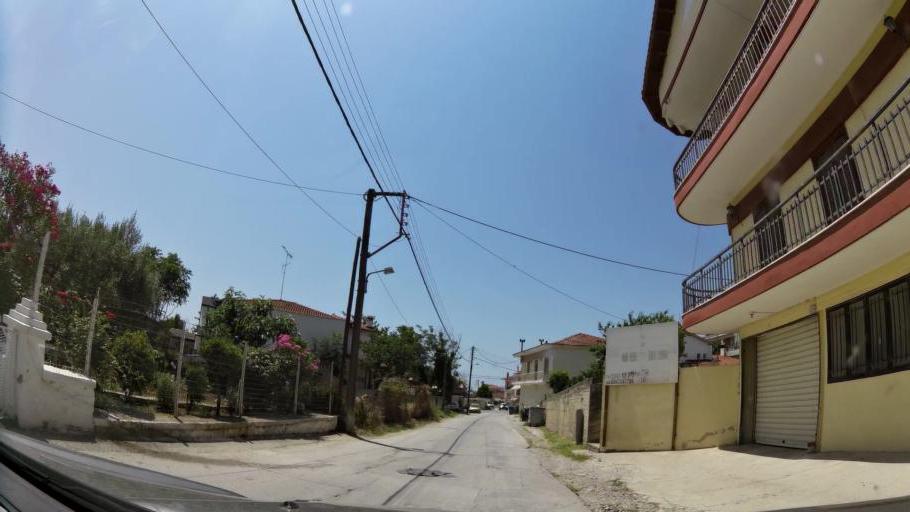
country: GR
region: Central Macedonia
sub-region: Nomos Thessalonikis
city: Epanomi
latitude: 40.4307
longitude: 22.9233
